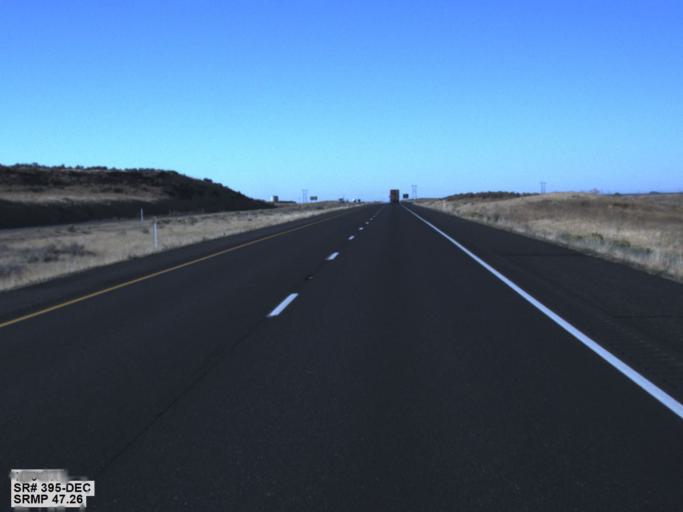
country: US
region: Washington
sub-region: Franklin County
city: Connell
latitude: 46.5813
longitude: -118.9732
